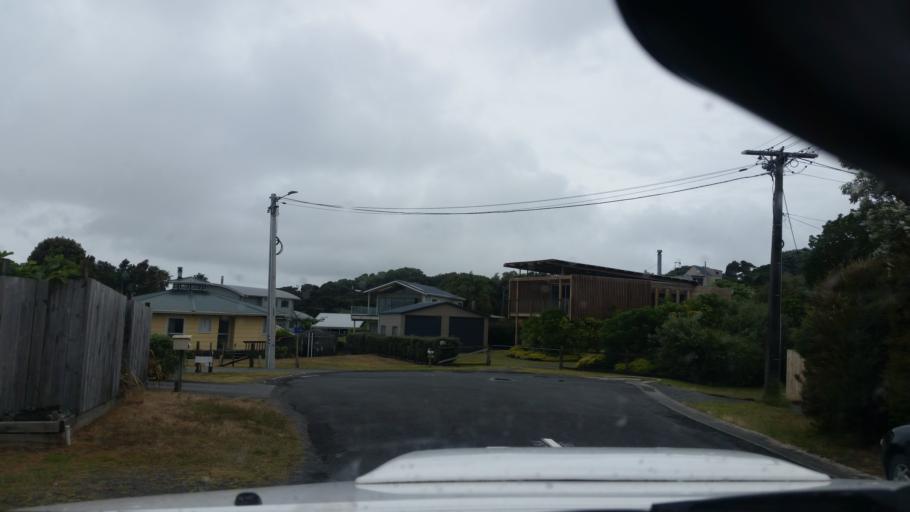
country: NZ
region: Auckland
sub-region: Auckland
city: Wellsford
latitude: -36.0990
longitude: 174.5892
